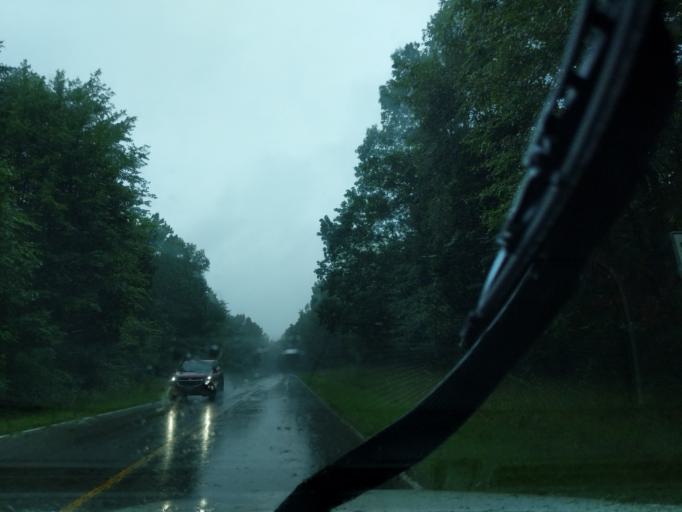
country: US
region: Kentucky
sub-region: Barren County
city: Cave City
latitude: 37.1419
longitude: -86.0862
